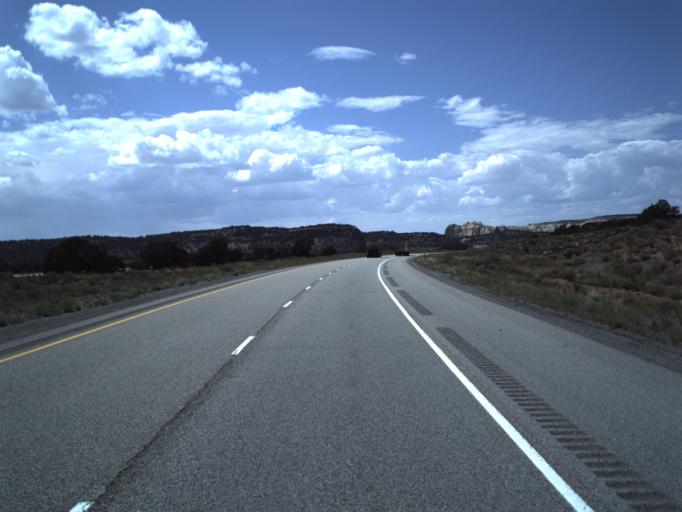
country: US
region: Utah
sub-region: Emery County
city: Castle Dale
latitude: 38.8675
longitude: -110.7130
